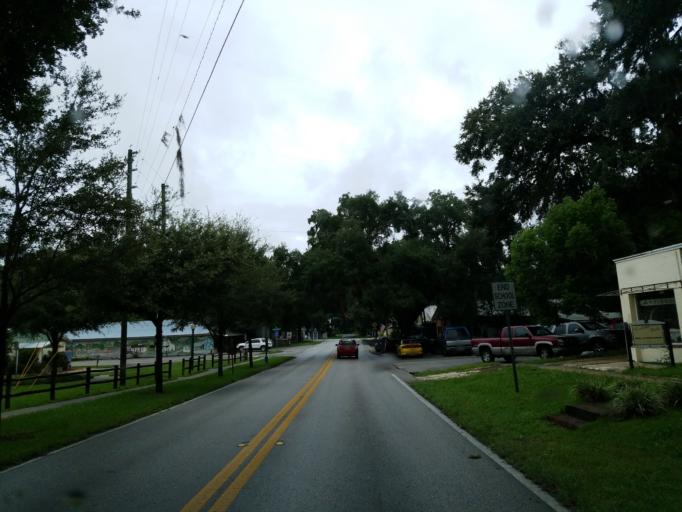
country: US
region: Florida
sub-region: Citrus County
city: Floral City
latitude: 28.7503
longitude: -82.2953
